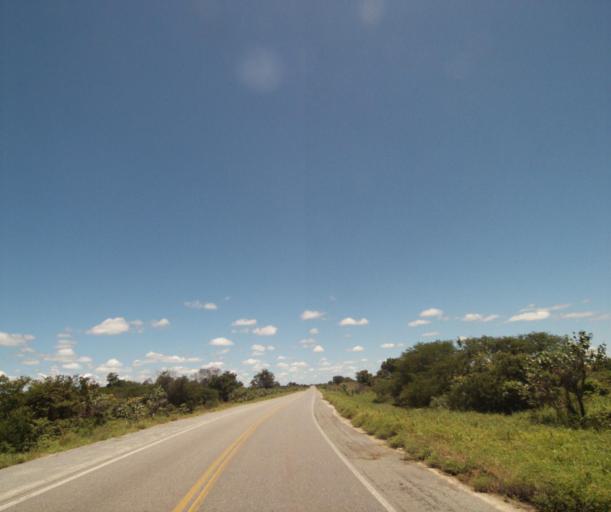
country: BR
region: Bahia
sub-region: Carinhanha
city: Carinhanha
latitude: -14.3142
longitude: -43.7850
